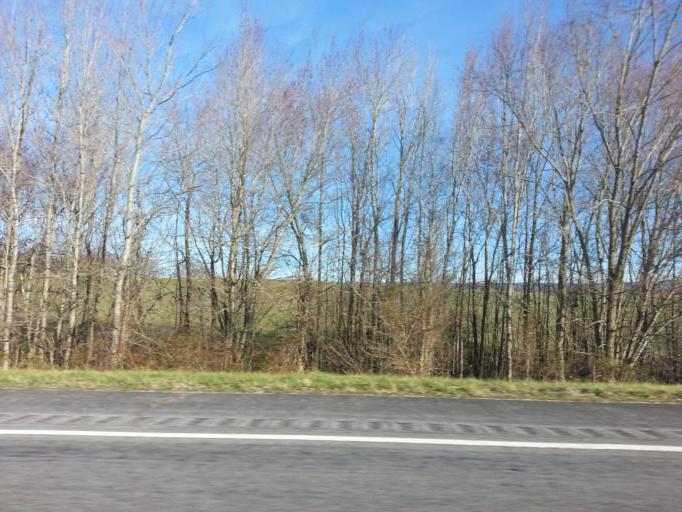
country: US
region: Tennessee
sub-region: Warren County
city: McMinnville
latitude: 35.7254
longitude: -85.6702
